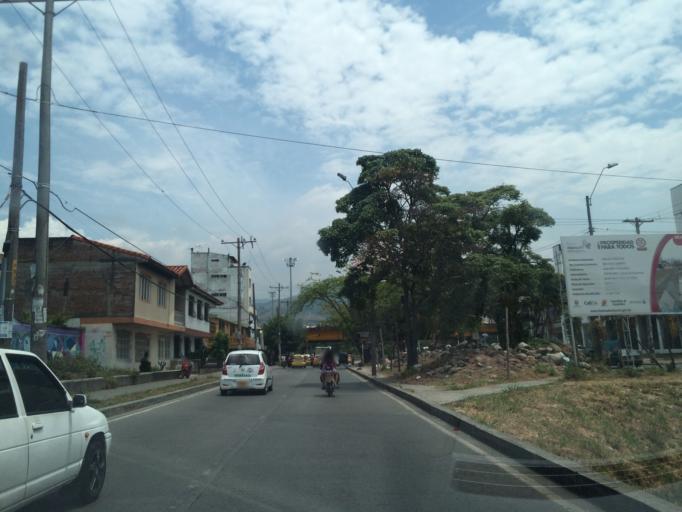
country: CO
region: Valle del Cauca
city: Cali
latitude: 3.4203
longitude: -76.5340
